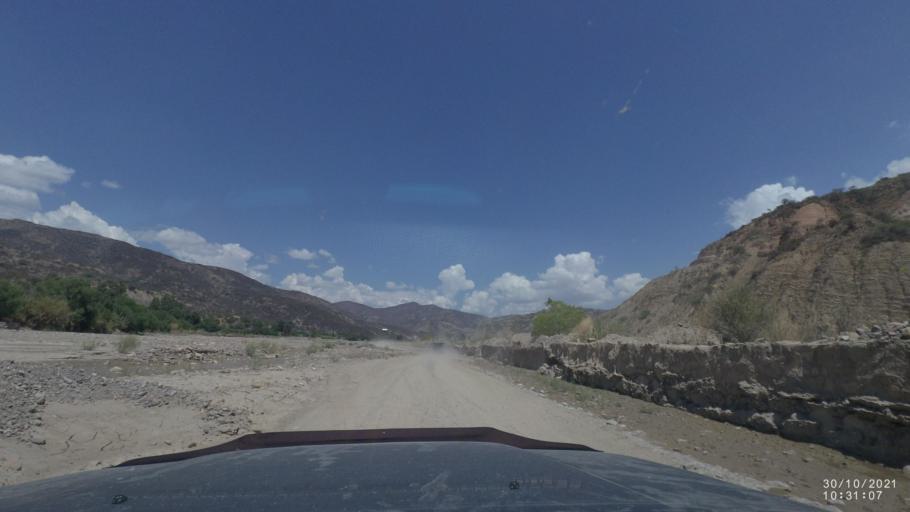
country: BO
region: Cochabamba
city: Sipe Sipe
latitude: -17.5473
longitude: -66.4057
